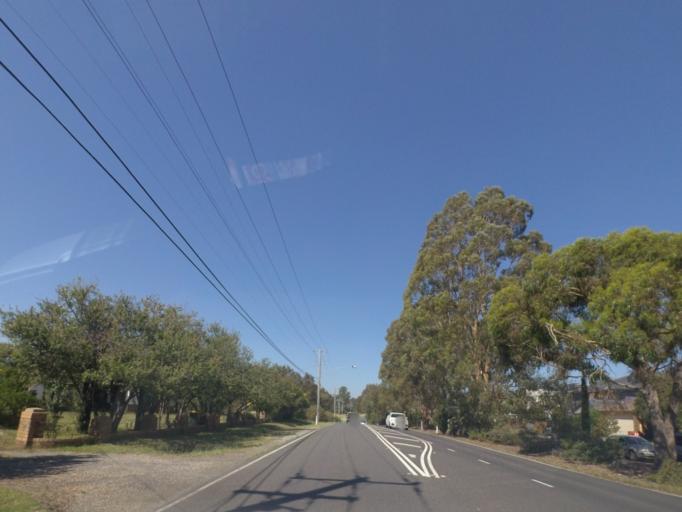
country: AU
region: Victoria
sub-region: Manningham
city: Bulleen
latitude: -37.7567
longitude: 145.0896
